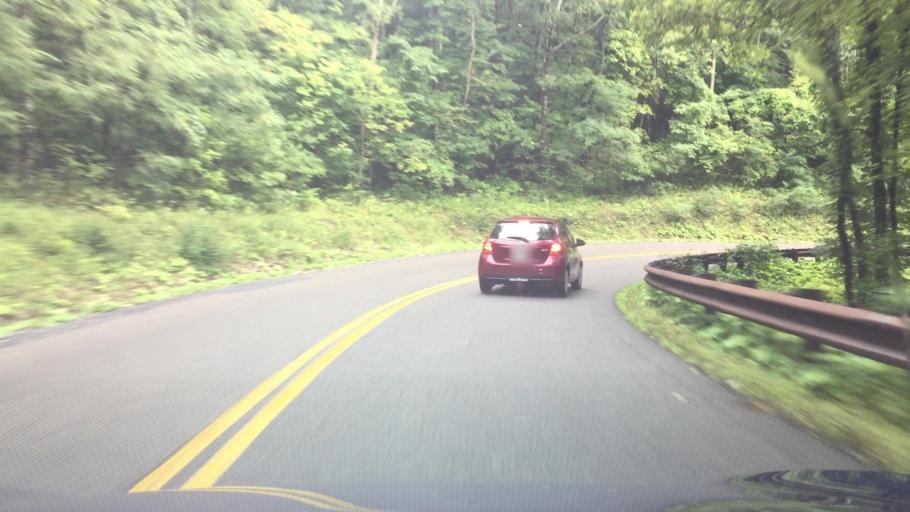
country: US
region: Virginia
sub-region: Smyth County
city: Atkins
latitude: 36.8146
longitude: -81.4067
